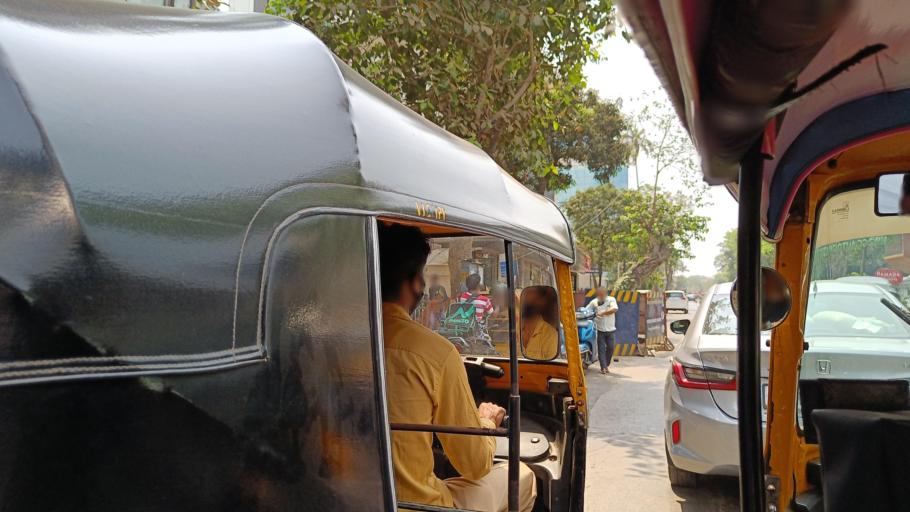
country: IN
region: Maharashtra
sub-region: Mumbai Suburban
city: Mumbai
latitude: 19.1016
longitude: 72.8272
